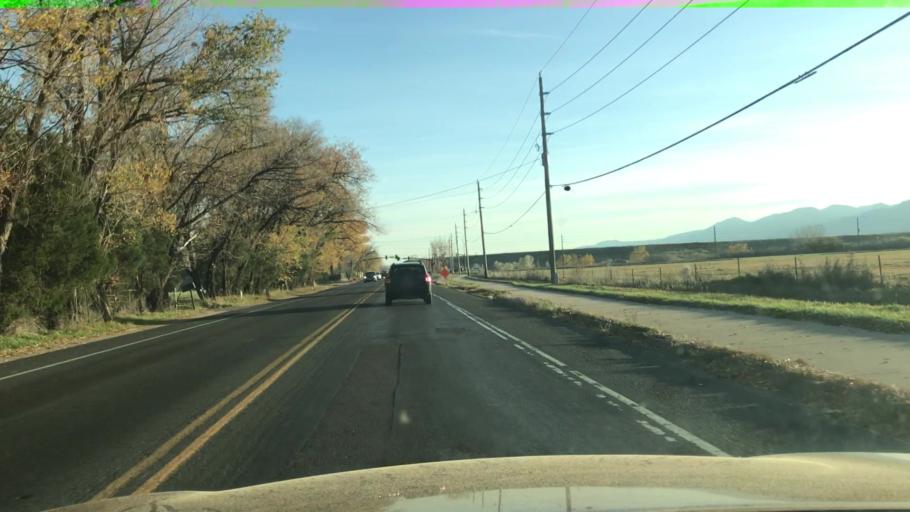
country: US
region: Colorado
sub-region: Boulder County
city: Gunbarrel
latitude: 40.0536
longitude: -105.2069
